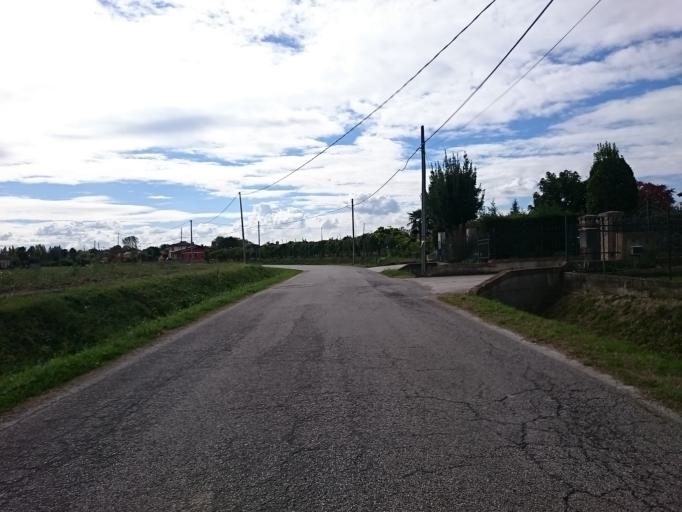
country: IT
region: Veneto
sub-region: Provincia di Padova
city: Bovolenta
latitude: 45.2510
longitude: 11.9369
